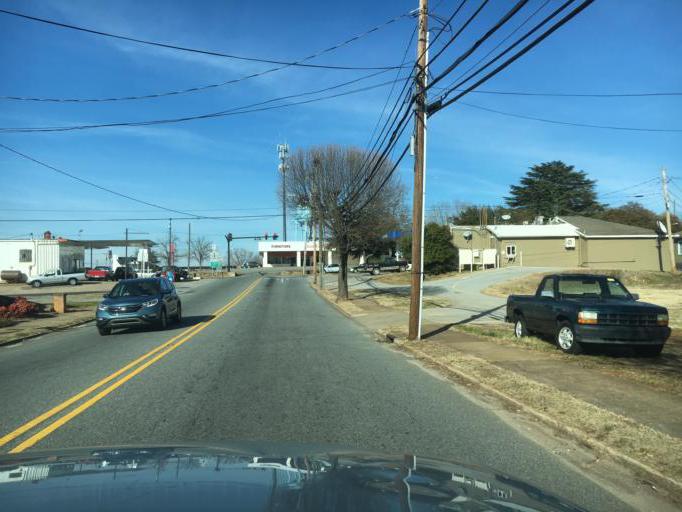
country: US
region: North Carolina
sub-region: Rutherford County
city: Forest City
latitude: 35.3321
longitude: -81.8622
